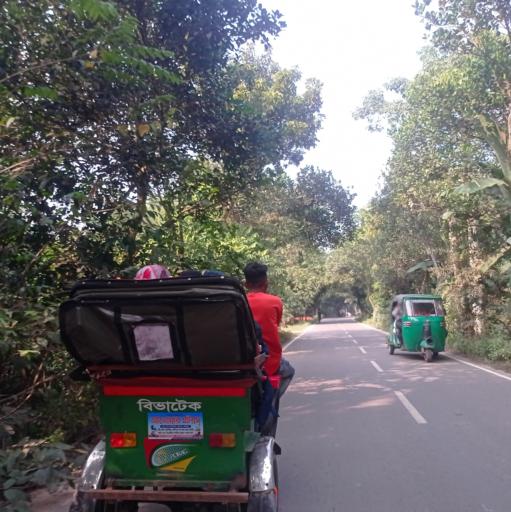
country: BD
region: Dhaka
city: Bhairab Bazar
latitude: 24.0870
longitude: 90.8498
